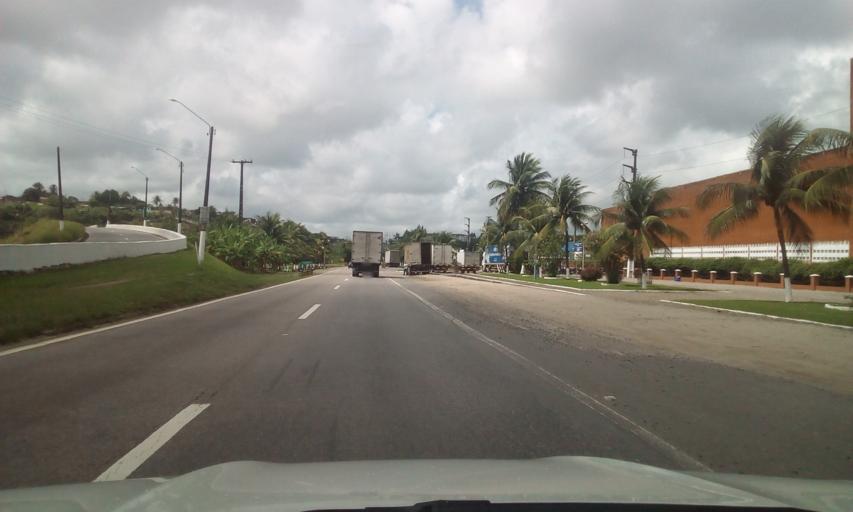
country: BR
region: Pernambuco
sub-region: Igarassu
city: Igarassu
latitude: -7.8322
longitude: -34.9139
